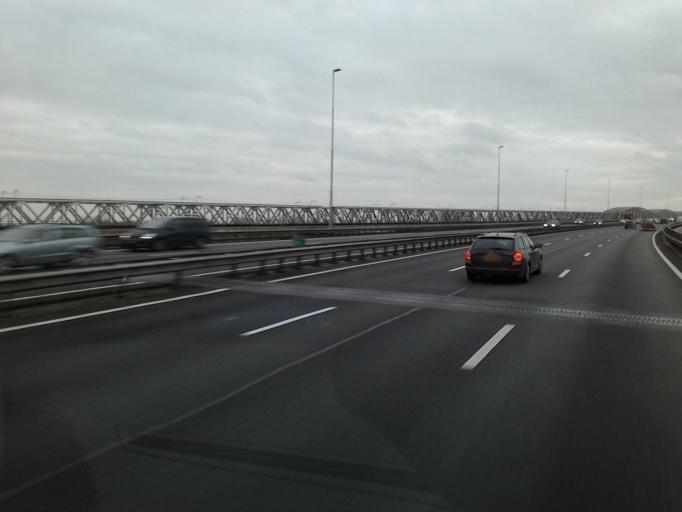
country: NL
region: Gelderland
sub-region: Gemeente Zaltbommel
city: Zaltbommel
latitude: 51.8253
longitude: 5.2581
